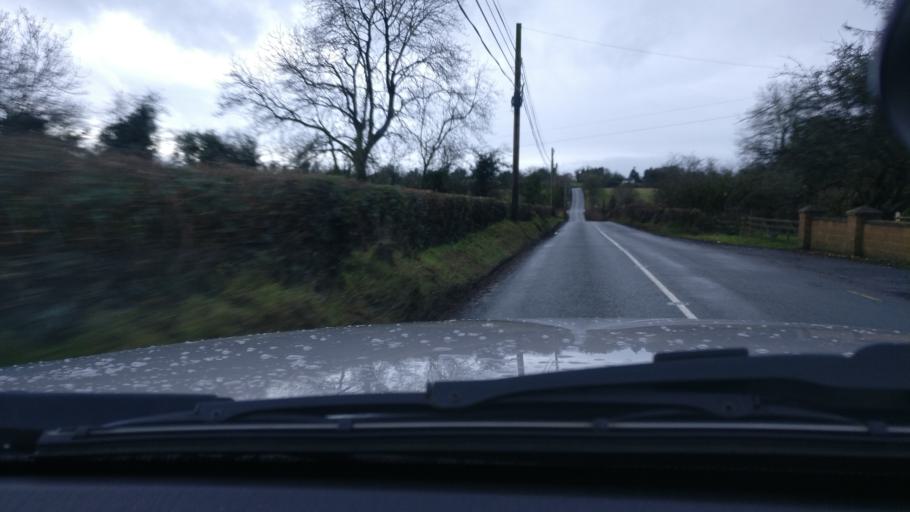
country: IE
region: Ulster
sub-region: An Cabhan
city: Ballyjamesduff
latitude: 53.8519
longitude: -7.2434
